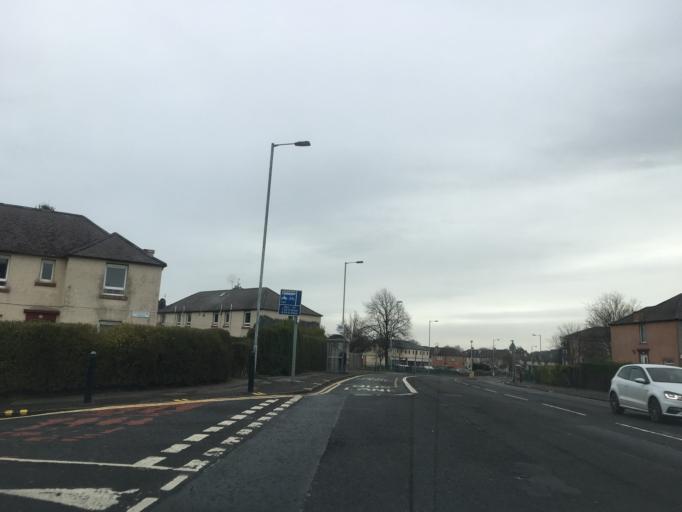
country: GB
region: Scotland
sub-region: Edinburgh
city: Colinton
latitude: 55.9336
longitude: -3.2637
